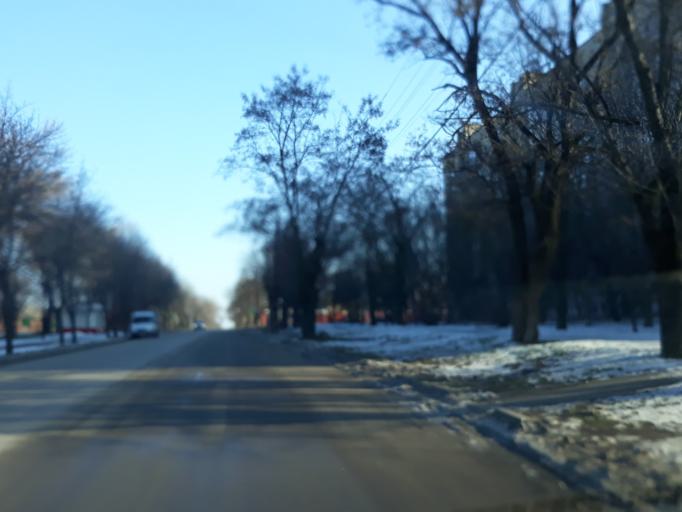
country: RU
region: Rostov
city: Taganrog
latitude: 47.2041
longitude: 38.9047
